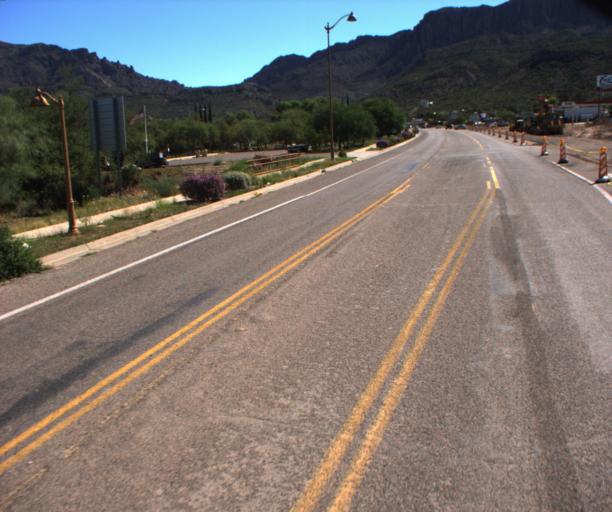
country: US
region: Arizona
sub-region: Pinal County
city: Superior
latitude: 33.2870
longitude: -111.1068
